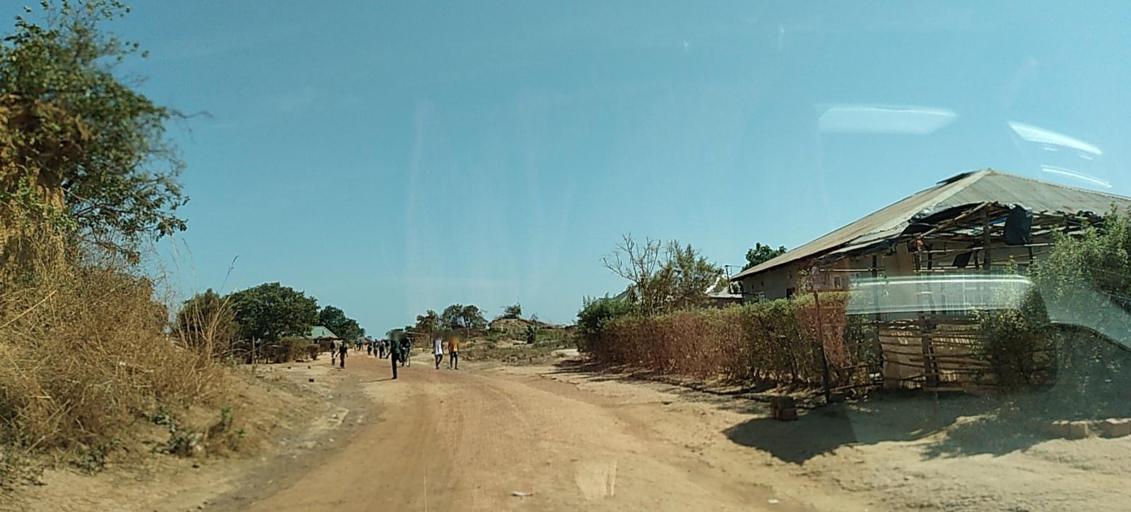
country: ZM
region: Copperbelt
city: Chililabombwe
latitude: -12.3247
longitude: 27.8604
